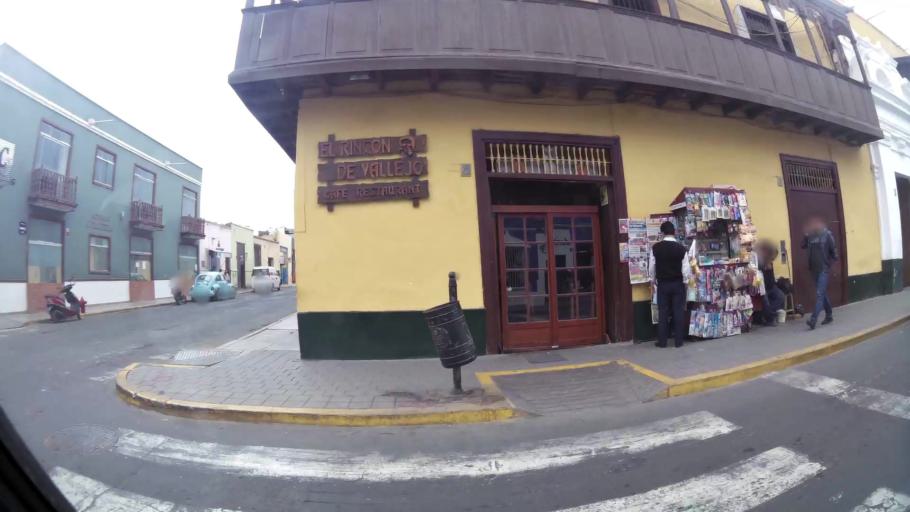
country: PE
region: La Libertad
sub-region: Provincia de Trujillo
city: Trujillo
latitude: -8.1100
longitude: -79.0296
